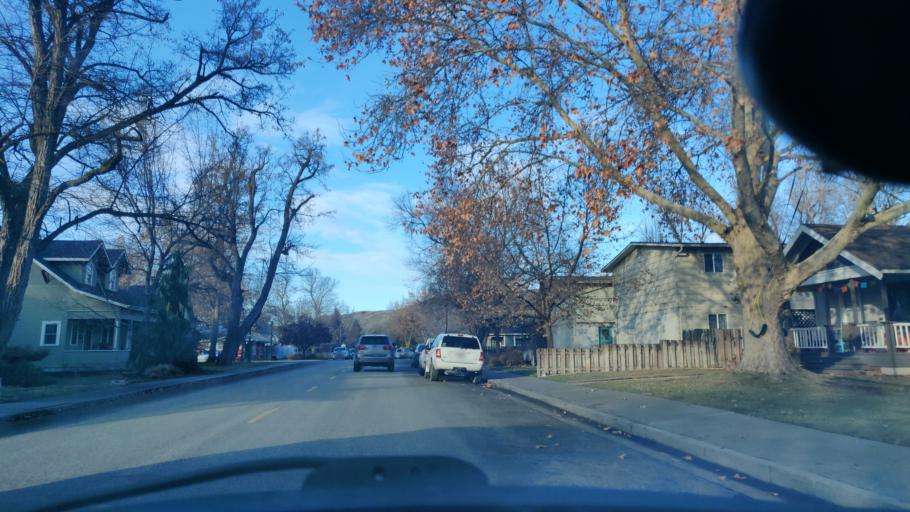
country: US
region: Idaho
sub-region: Ada County
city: Boise
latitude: 43.6322
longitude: -116.2034
